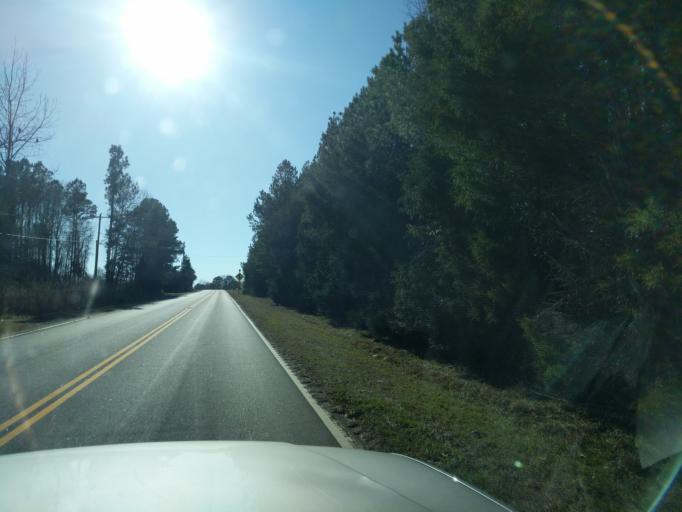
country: US
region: South Carolina
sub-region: Anderson County
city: Homeland Park
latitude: 34.4316
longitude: -82.7454
